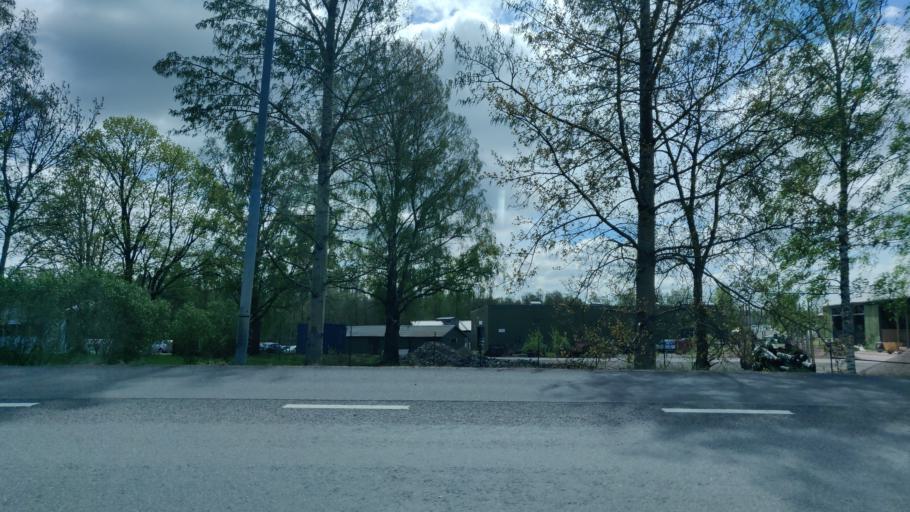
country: SE
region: Vaermland
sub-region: Karlstads Kommun
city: Molkom
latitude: 59.5971
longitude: 13.7288
